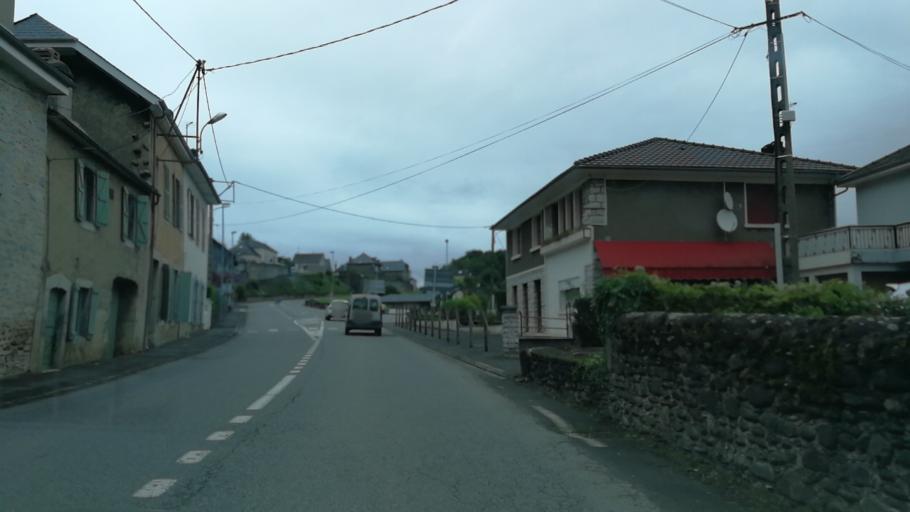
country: FR
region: Aquitaine
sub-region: Departement des Pyrenees-Atlantiques
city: Oloron-Sainte-Marie
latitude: 43.1214
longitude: -0.6137
